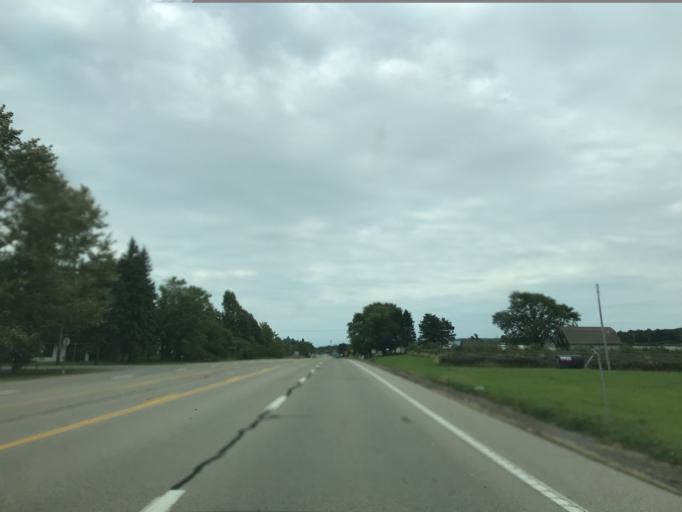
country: US
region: Pennsylvania
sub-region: Erie County
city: North East
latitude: 42.2288
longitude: -79.7932
